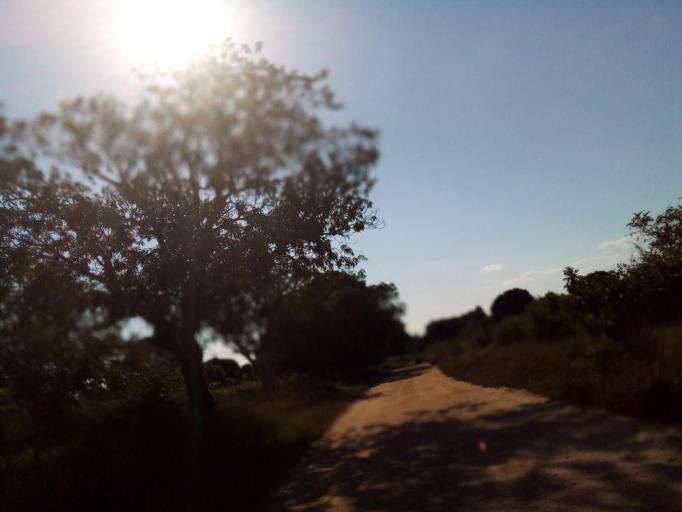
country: MZ
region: Zambezia
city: Quelimane
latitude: -17.5283
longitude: 36.6176
